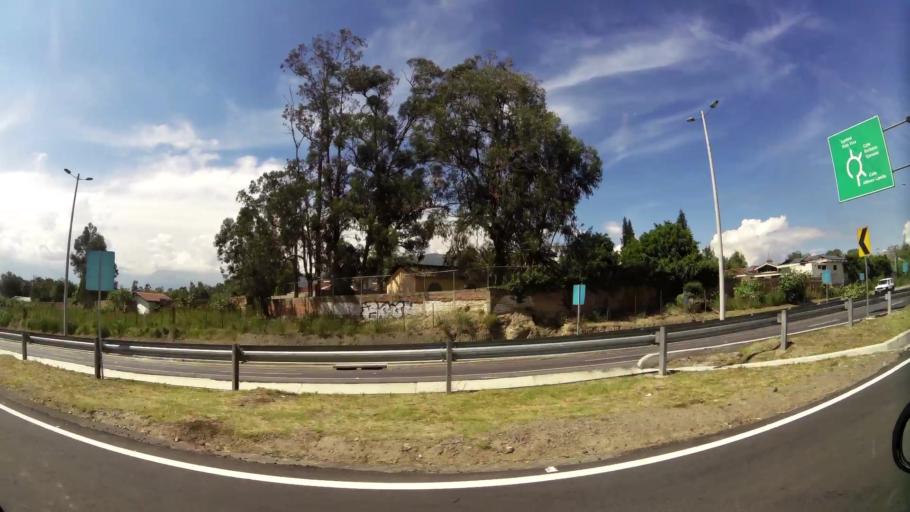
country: EC
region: Pichincha
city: Quito
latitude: -0.2112
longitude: -78.4399
